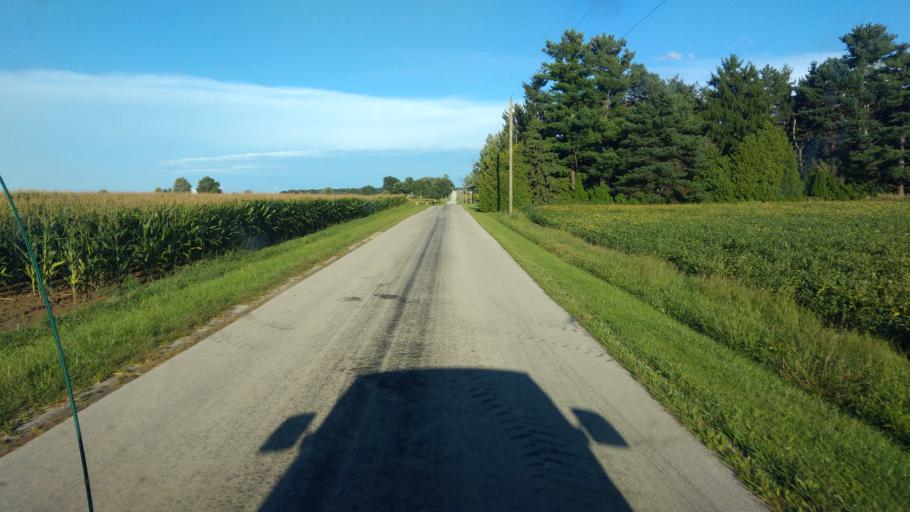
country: US
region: Ohio
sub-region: Wyandot County
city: Upper Sandusky
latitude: 40.8470
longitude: -83.3410
